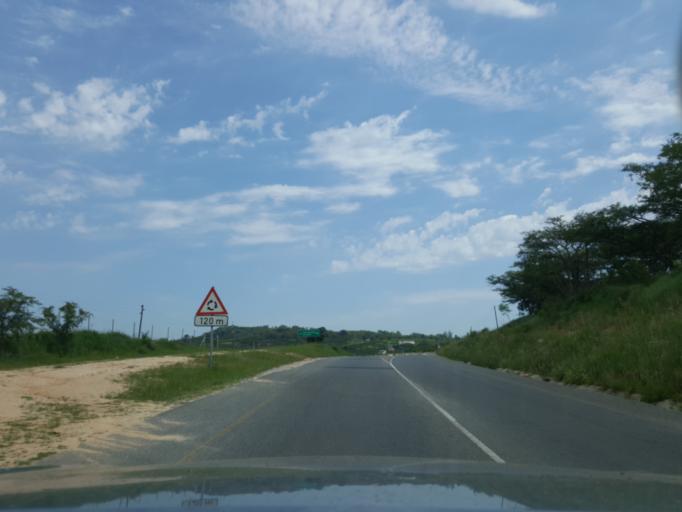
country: ZA
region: Mpumalanga
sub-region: Ehlanzeni District
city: White River
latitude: -25.3800
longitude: 31.0821
